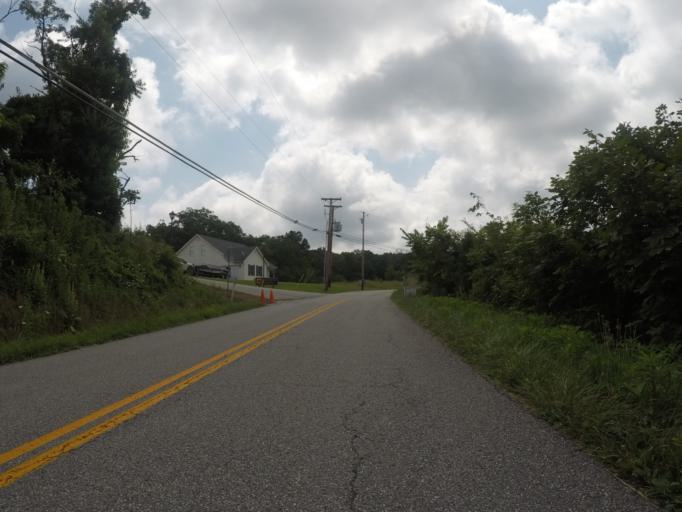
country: US
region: Kentucky
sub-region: Boyd County
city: Catlettsburg
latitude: 38.4021
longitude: -82.6430
